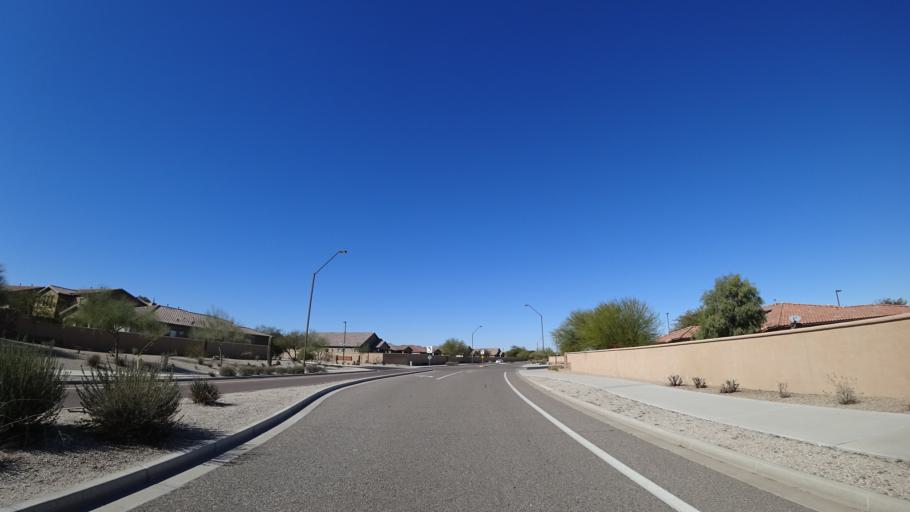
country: US
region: Arizona
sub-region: Maricopa County
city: Goodyear
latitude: 33.3245
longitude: -112.4459
